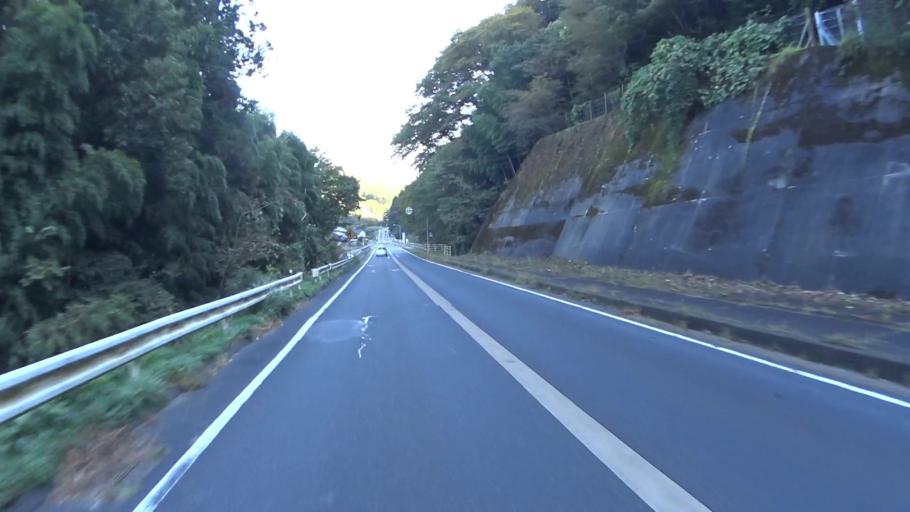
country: JP
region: Kyoto
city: Fukuchiyama
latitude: 35.3966
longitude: 135.0879
